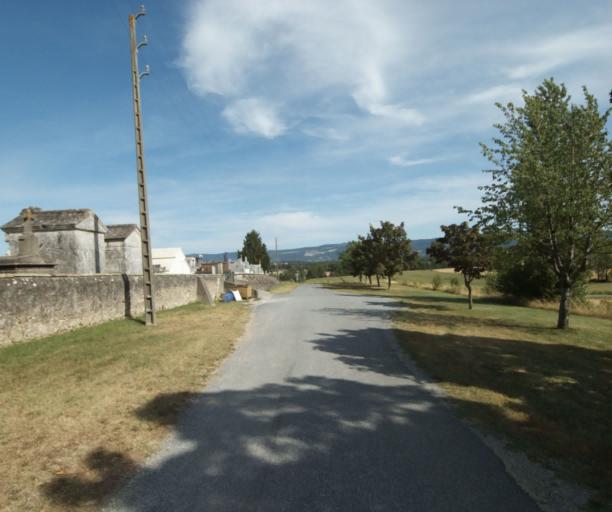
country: FR
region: Midi-Pyrenees
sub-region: Departement du Tarn
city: Puylaurens
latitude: 43.5243
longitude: 2.0555
